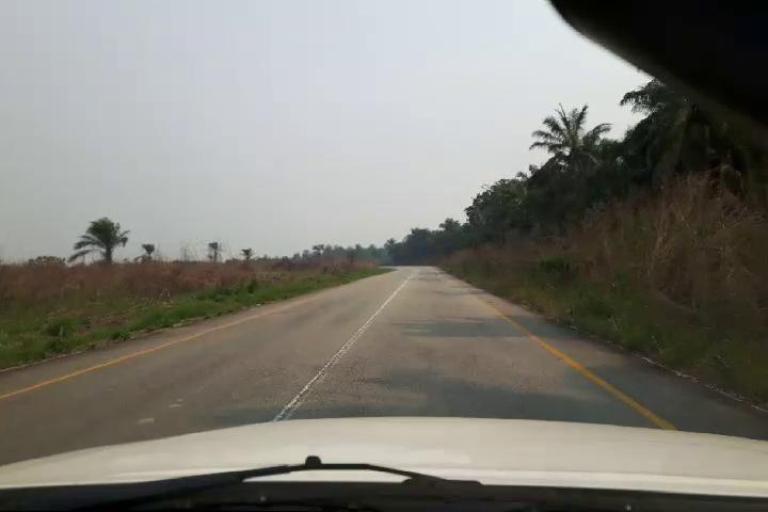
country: SL
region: Southern Province
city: Largo
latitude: 8.2158
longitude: -12.0741
